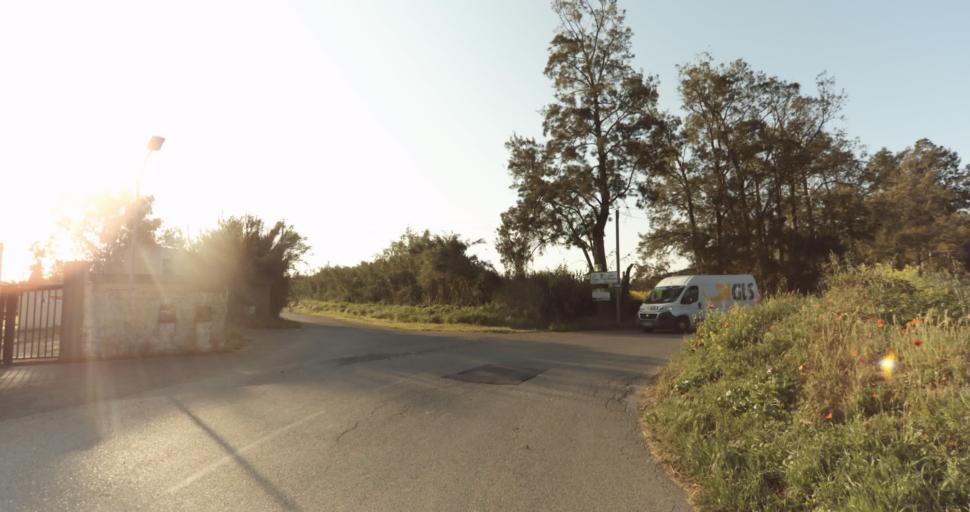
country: FR
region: Corsica
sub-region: Departement de la Haute-Corse
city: Biguglia
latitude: 42.6152
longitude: 9.4438
